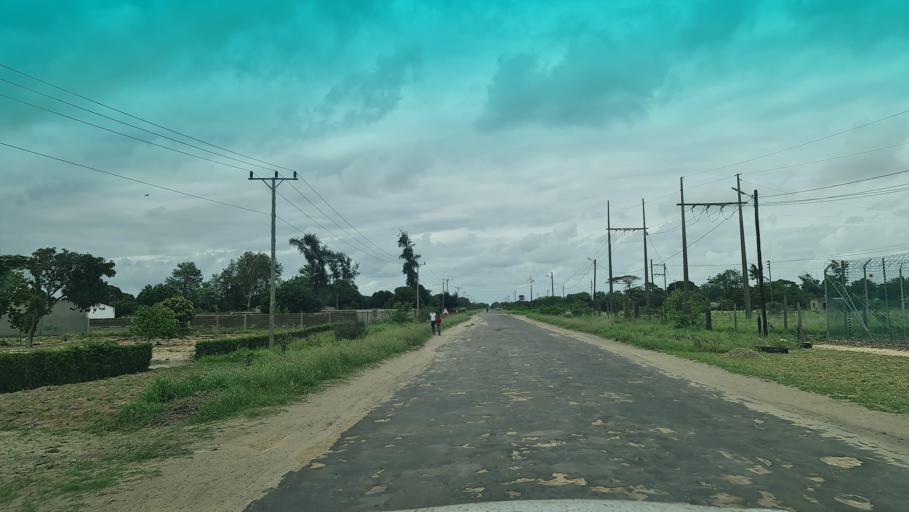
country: MZ
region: Maputo
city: Manhica
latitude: -25.4331
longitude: 32.7731
